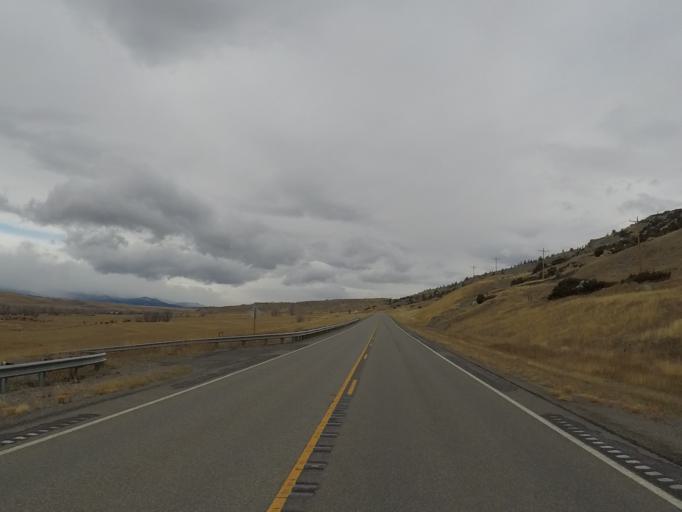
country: US
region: Montana
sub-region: Sweet Grass County
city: Big Timber
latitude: 45.8877
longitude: -109.9588
